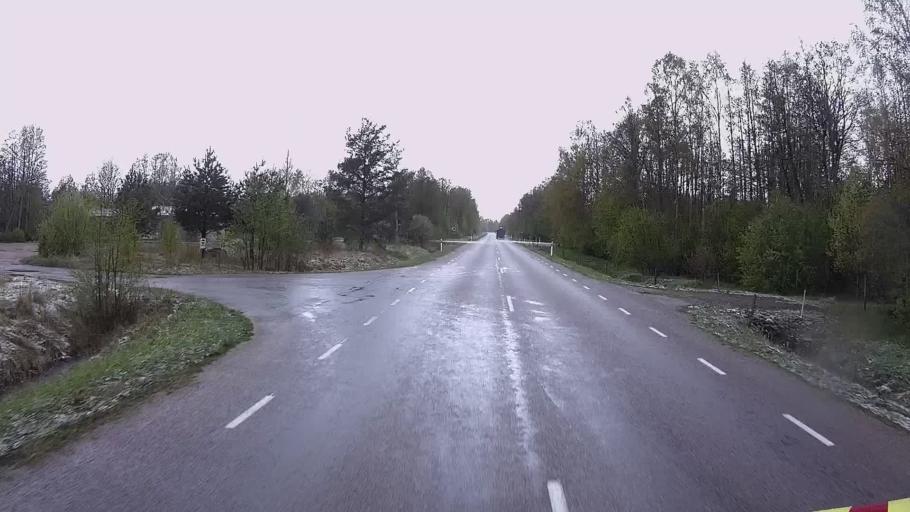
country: EE
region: Hiiumaa
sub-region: Kaerdla linn
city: Kardla
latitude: 58.7871
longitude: 22.4915
